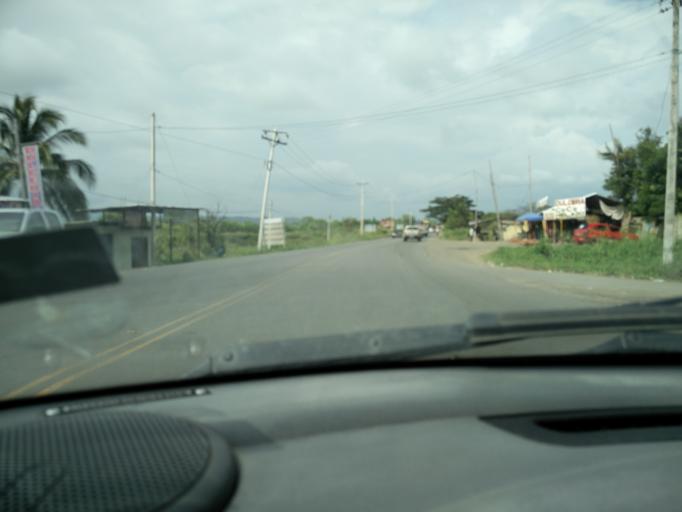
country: EC
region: Manabi
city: Rocafuerte
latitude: -0.9253
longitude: -80.4786
